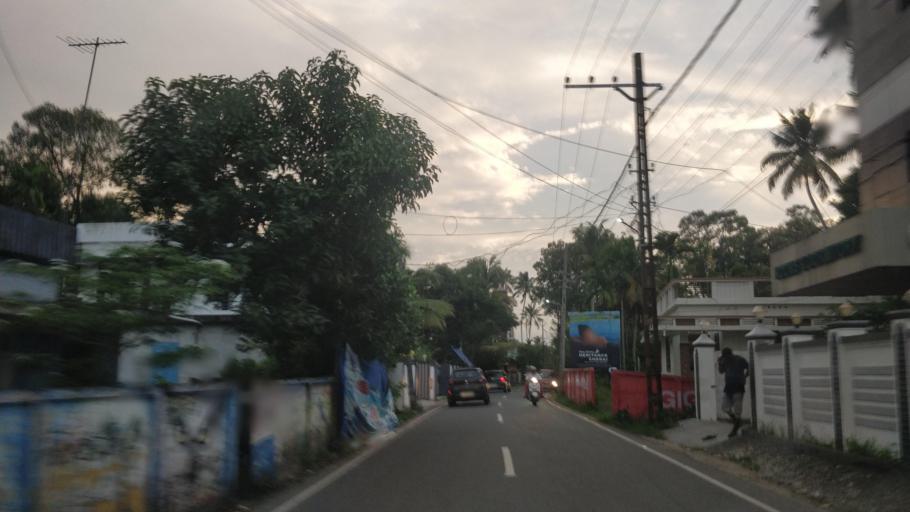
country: IN
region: Kerala
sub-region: Thrissur District
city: Kodungallur
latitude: 10.1411
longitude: 76.1879
